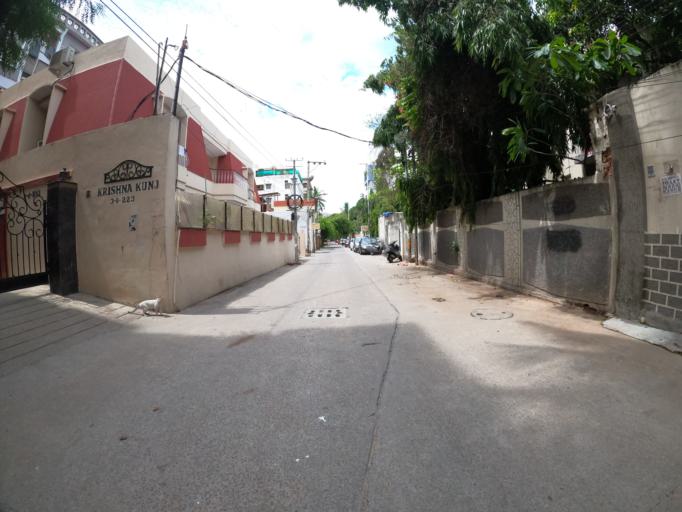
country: IN
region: Telangana
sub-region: Hyderabad
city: Hyderabad
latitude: 17.3986
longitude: 78.4841
